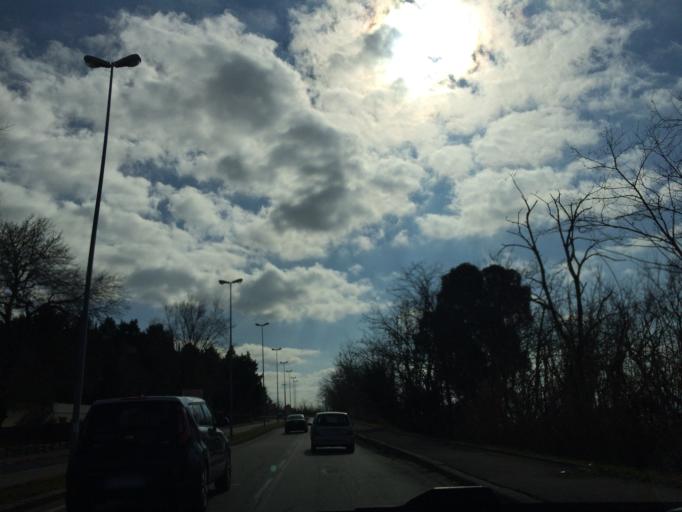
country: IT
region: Basilicate
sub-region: Provincia di Matera
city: Matera
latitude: 40.6691
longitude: 16.5894
